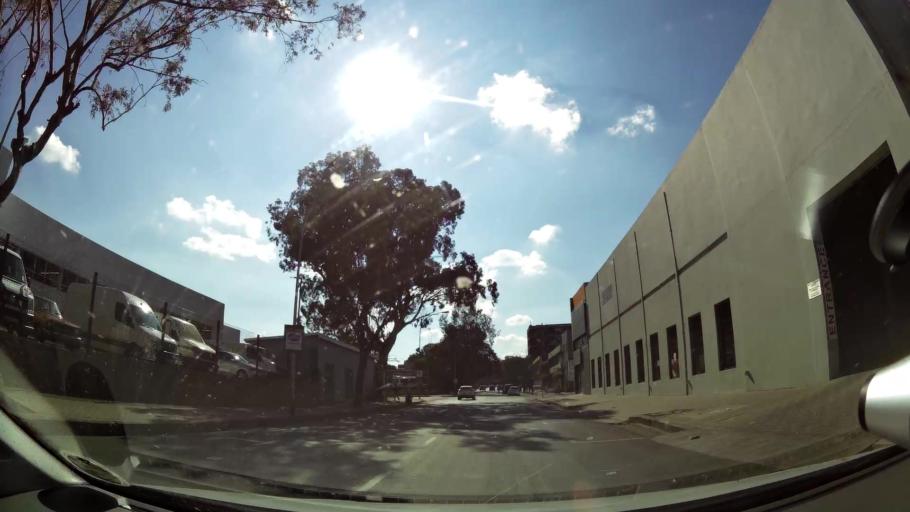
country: ZA
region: Orange Free State
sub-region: Mangaung Metropolitan Municipality
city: Bloemfontein
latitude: -29.1121
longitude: 26.2218
